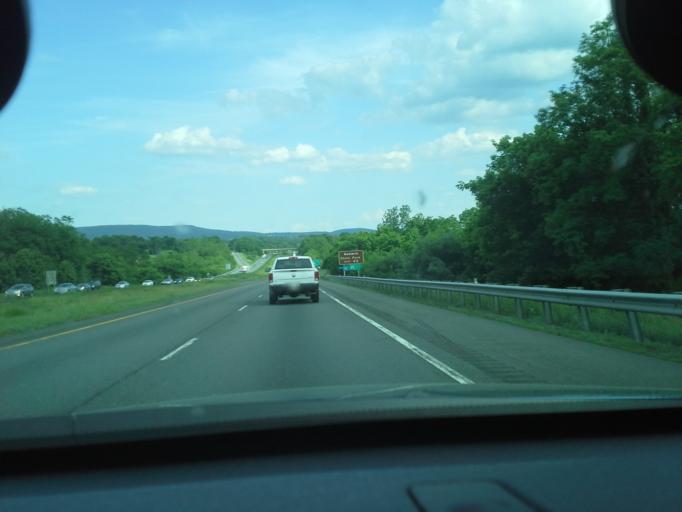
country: US
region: Maryland
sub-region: Frederick County
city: Myersville
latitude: 39.5017
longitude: -77.5765
